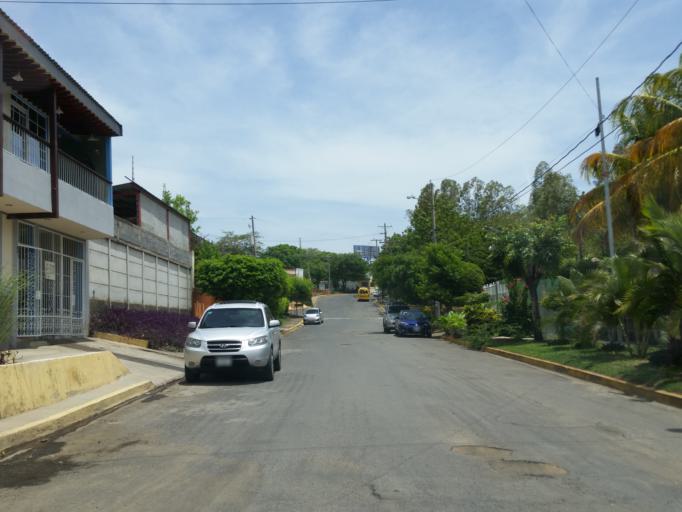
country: NI
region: Managua
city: Managua
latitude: 12.1087
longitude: -86.2461
